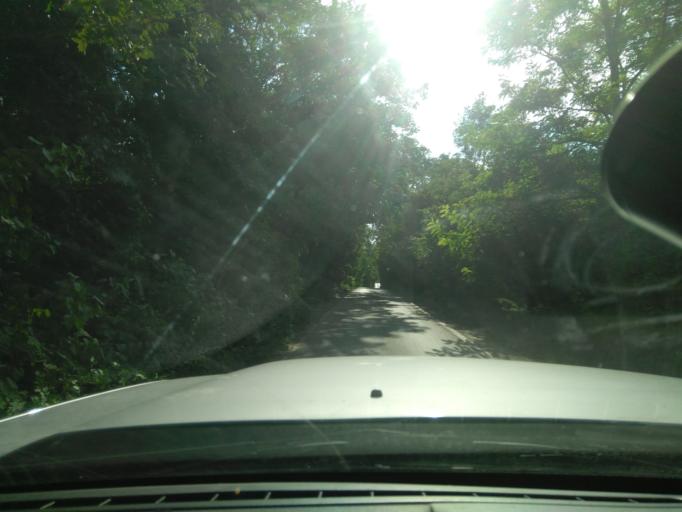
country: HU
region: Fejer
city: Bicske
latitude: 47.4962
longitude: 18.6514
